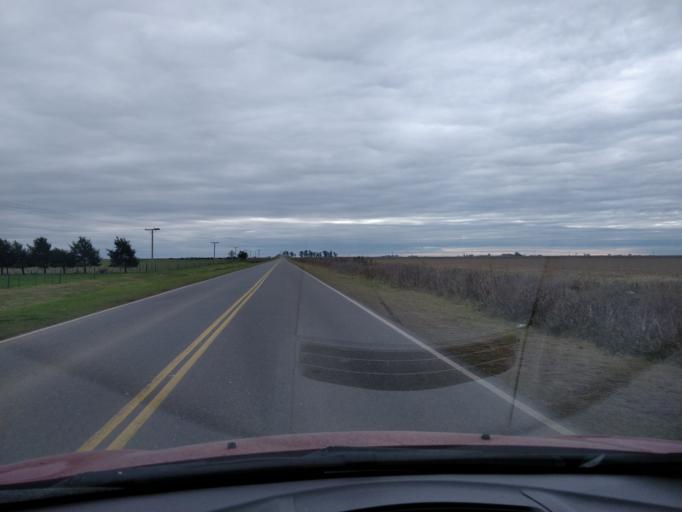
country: AR
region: Cordoba
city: Leones
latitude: -32.6400
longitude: -62.2897
